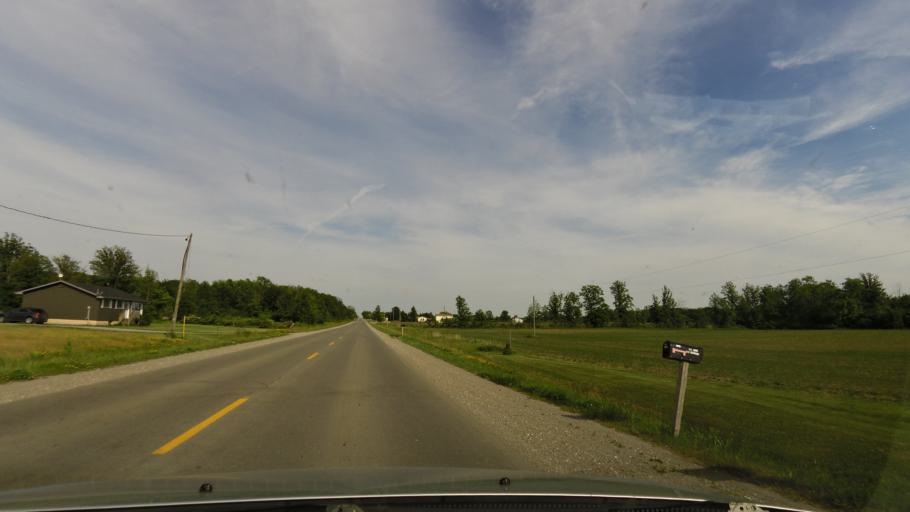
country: CA
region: Ontario
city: Ancaster
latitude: 43.0543
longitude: -80.0792
